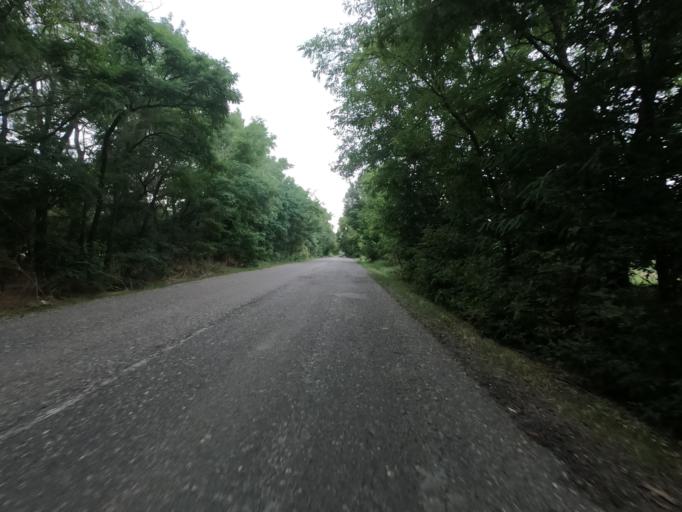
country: HU
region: Heves
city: Poroszlo
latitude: 47.7019
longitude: 20.6404
